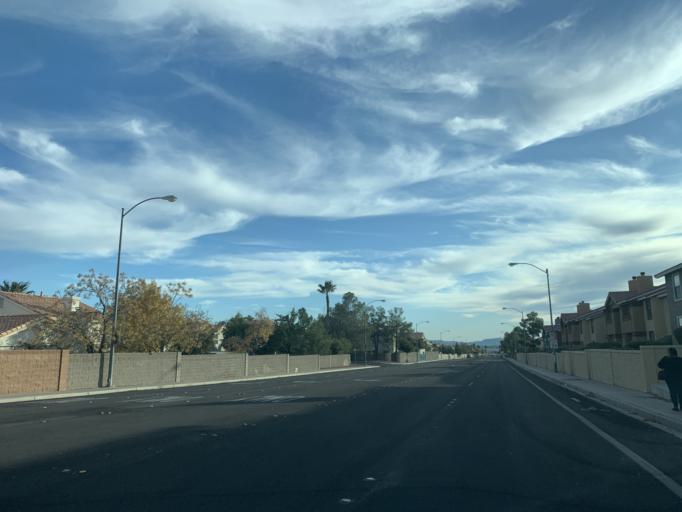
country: US
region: Nevada
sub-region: Clark County
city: Summerlin South
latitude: 36.1295
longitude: -115.2880
